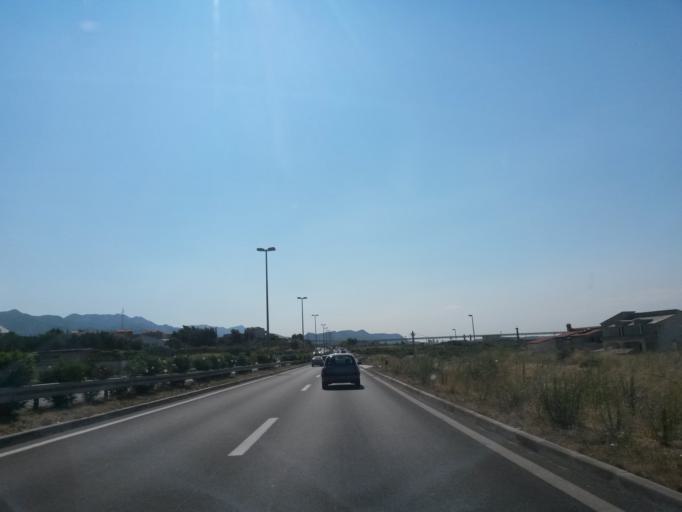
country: HR
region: Splitsko-Dalmatinska
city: Vranjic
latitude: 43.5484
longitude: 16.4413
